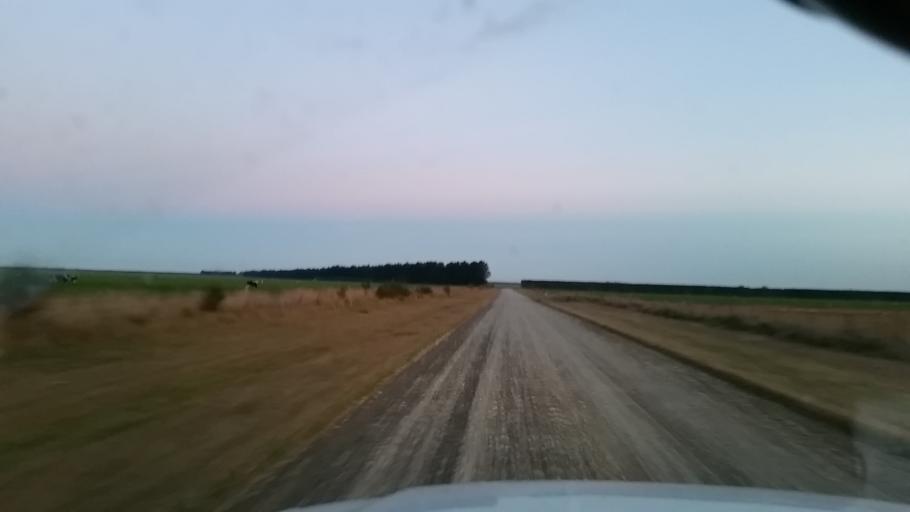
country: NZ
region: Canterbury
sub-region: Ashburton District
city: Tinwald
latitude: -43.9411
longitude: 171.6102
